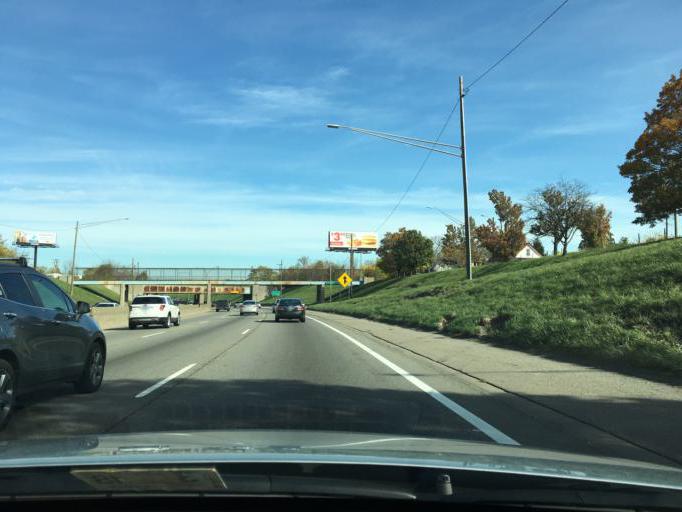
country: US
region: Michigan
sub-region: Wayne County
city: Hamtramck
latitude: 42.3925
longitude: -82.9945
